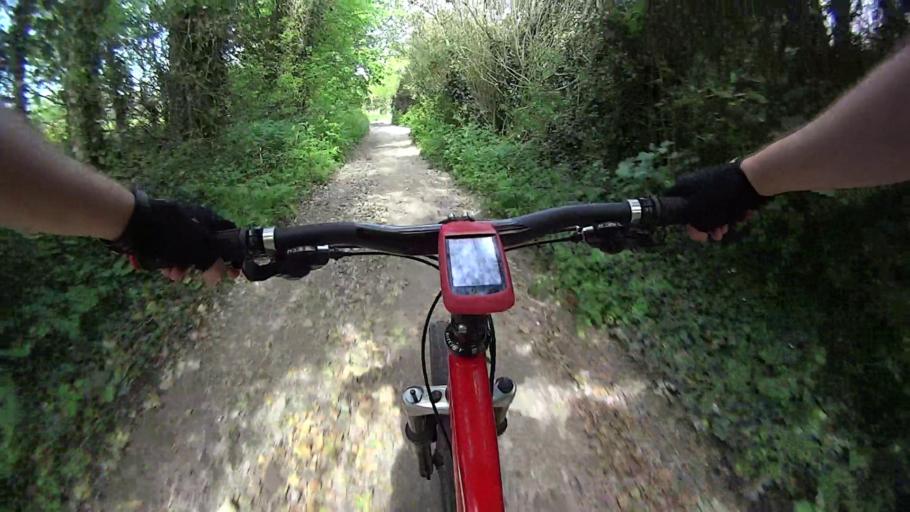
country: GB
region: England
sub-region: East Sussex
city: Seaford
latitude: 50.8104
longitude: 0.1658
